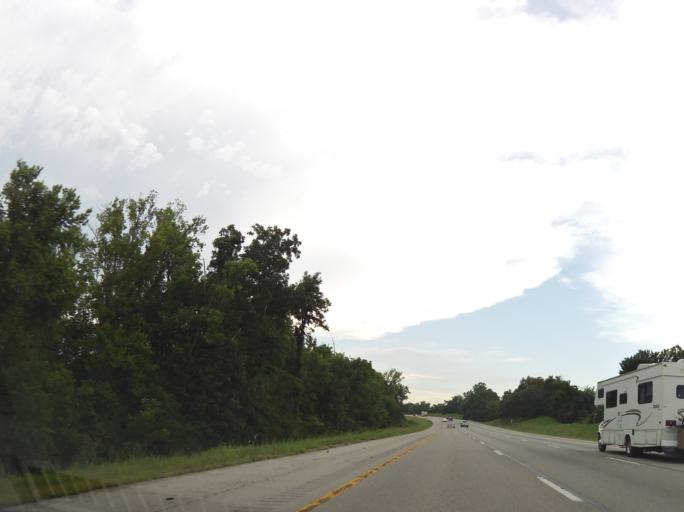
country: US
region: Kentucky
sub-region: Madison County
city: Richmond
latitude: 37.6609
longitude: -84.3103
